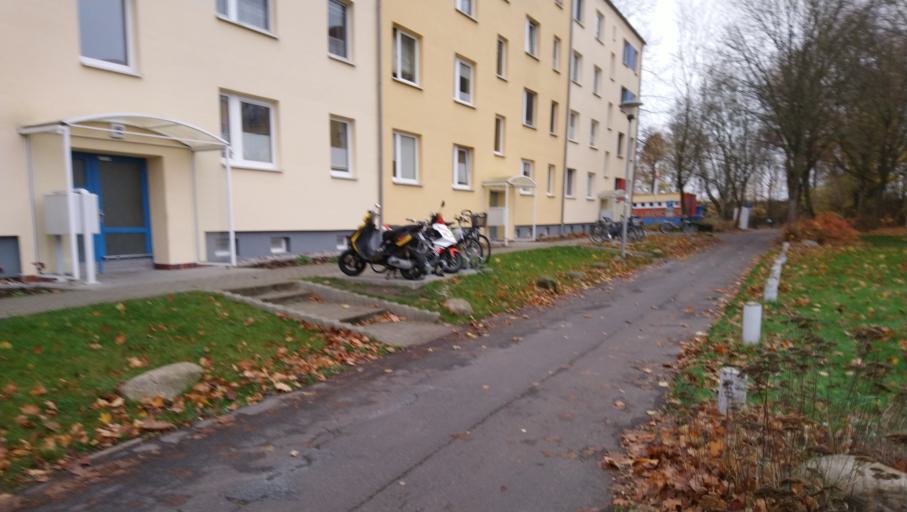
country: DE
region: Mecklenburg-Vorpommern
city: Kritzmow
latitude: 54.0982
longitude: 12.0675
